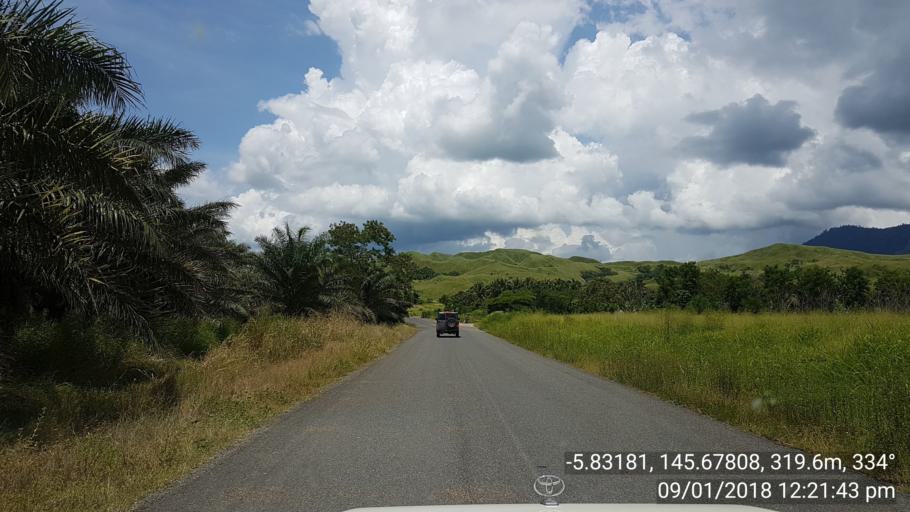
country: PG
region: Eastern Highlands
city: Goroka
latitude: -5.8318
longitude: 145.6784
